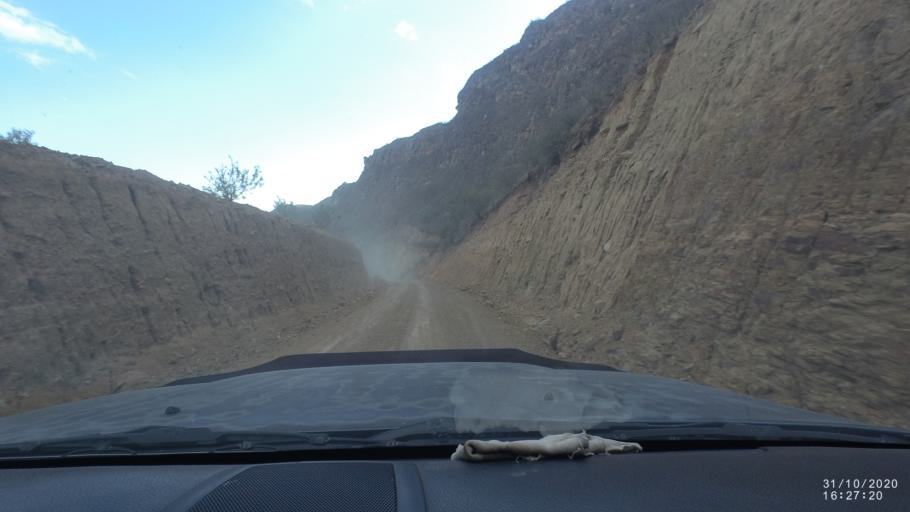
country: BO
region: Chuquisaca
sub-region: Provincia Zudanez
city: Mojocoya
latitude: -18.4055
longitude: -64.5858
